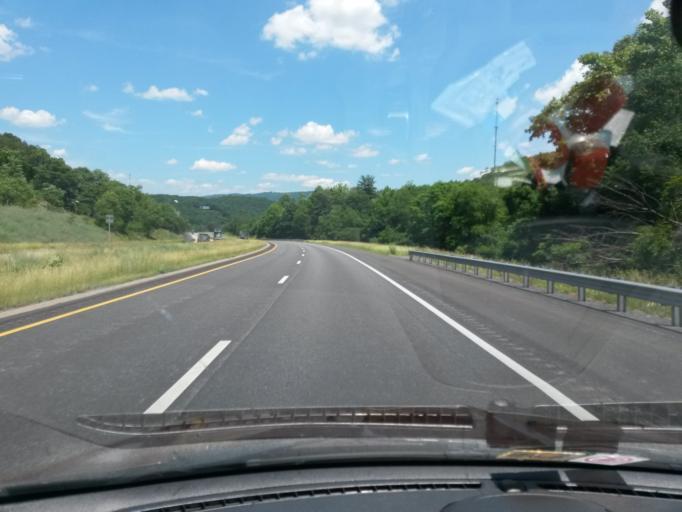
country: US
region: Virginia
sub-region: City of Covington
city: Covington
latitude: 37.8153
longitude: -80.1239
